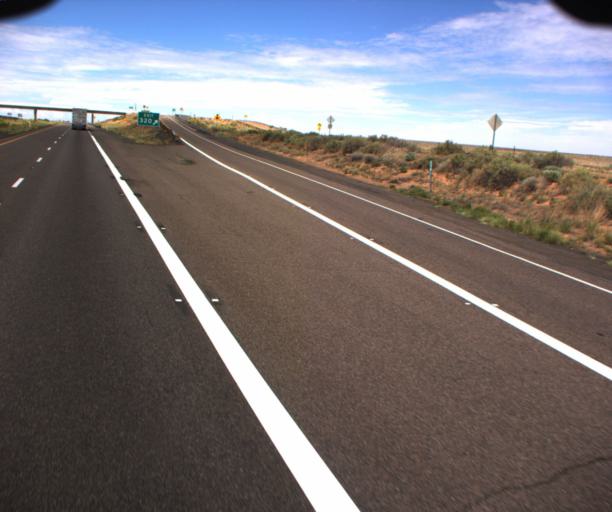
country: US
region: Arizona
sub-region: Apache County
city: Houck
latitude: 35.1000
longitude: -109.6383
